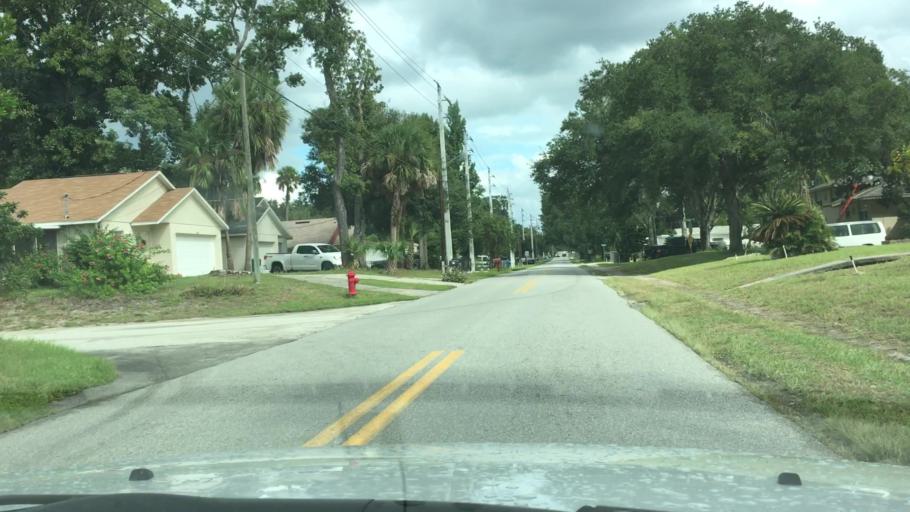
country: US
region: Florida
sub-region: Volusia County
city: Holly Hill
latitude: 29.2366
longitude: -81.0445
